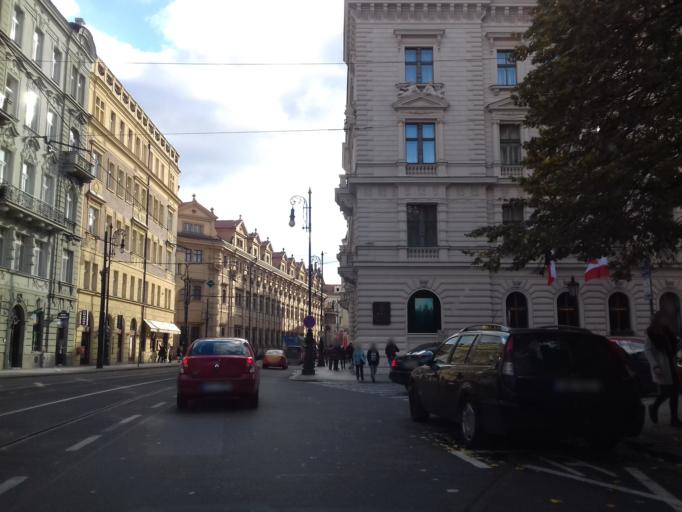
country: CZ
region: Praha
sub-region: Praha 1
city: Stare Mesto
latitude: 50.0878
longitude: 14.4151
